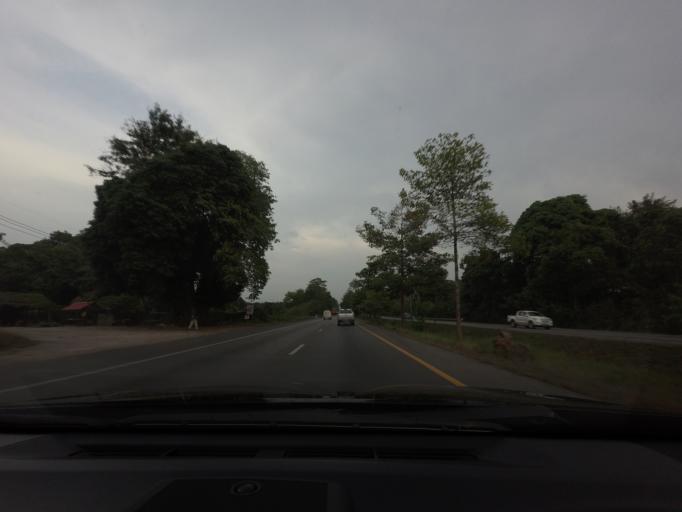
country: TH
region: Surat Thani
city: Tha Chana
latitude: 9.4833
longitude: 99.1419
